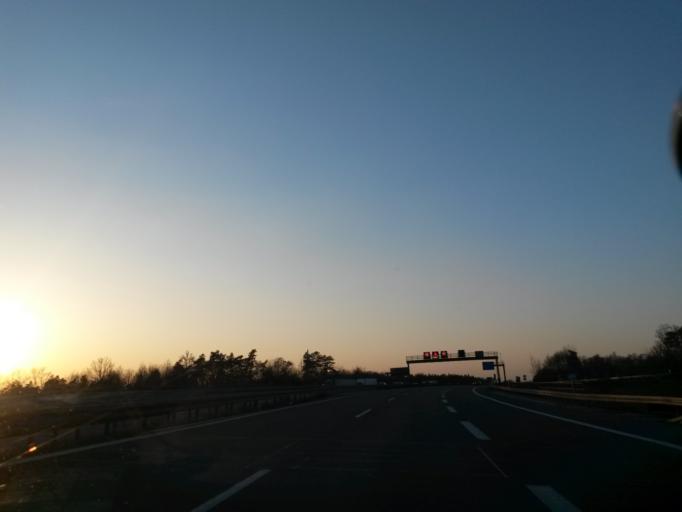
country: DE
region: Bavaria
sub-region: Regierungsbezirk Mittelfranken
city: Wendelstein
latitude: 49.3760
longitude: 11.1398
